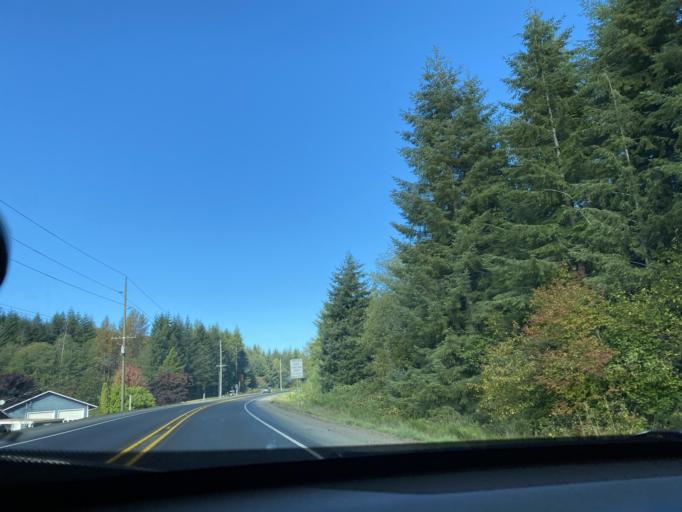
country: US
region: Washington
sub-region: Clallam County
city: Forks
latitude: 47.9630
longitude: -124.3992
